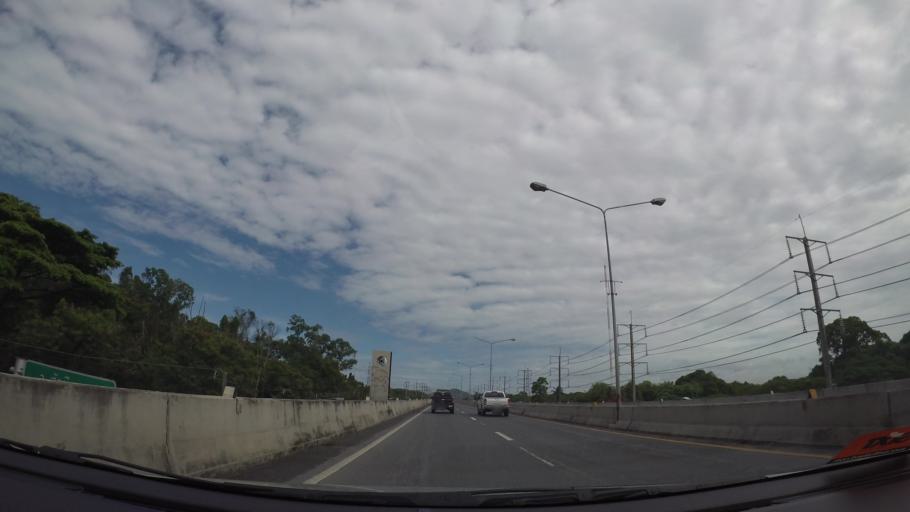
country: TH
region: Rayong
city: Ban Chang
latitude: 12.7274
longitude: 101.1443
